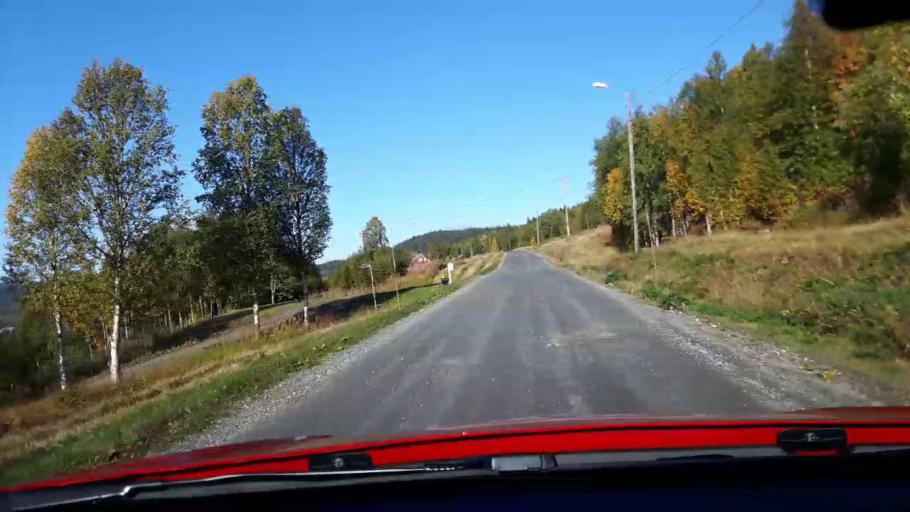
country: NO
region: Nord-Trondelag
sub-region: Lierne
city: Sandvika
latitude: 64.6062
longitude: 13.7795
